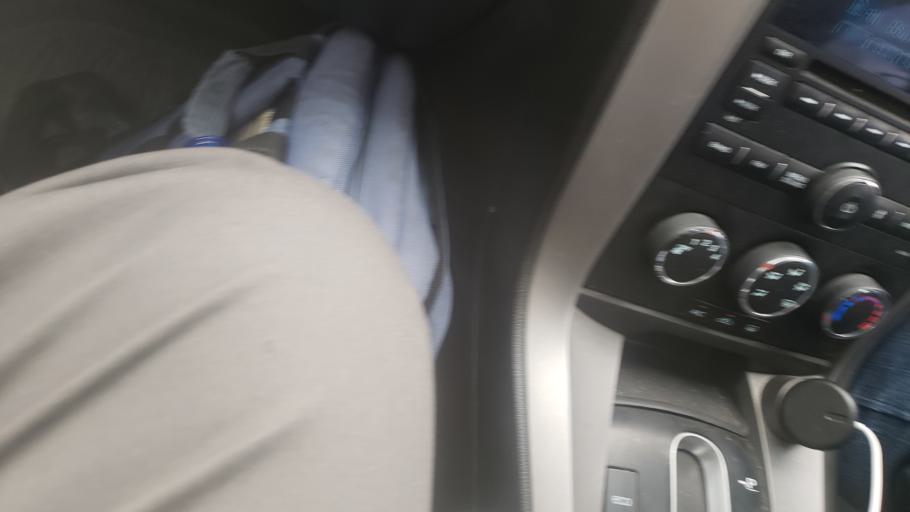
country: NZ
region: Otago
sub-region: Dunedin City
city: Dunedin
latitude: -45.9227
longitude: 170.4175
